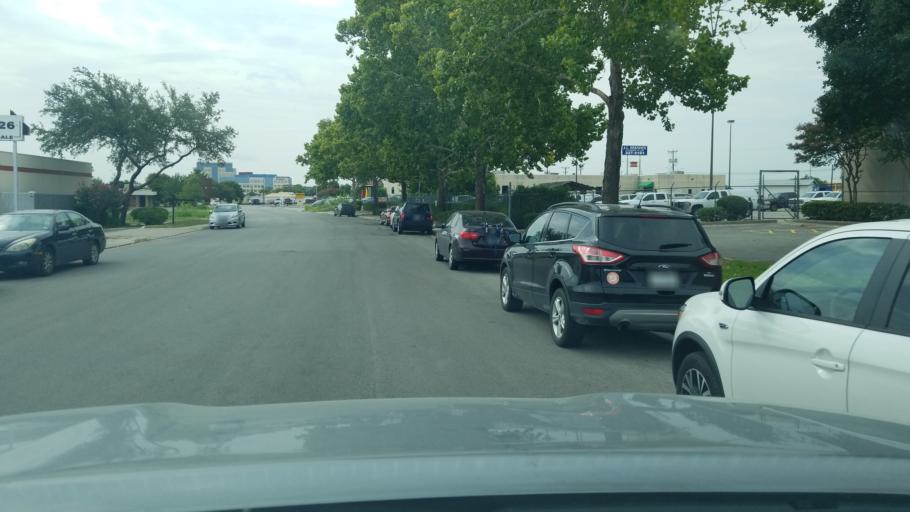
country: US
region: Texas
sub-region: Bexar County
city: Castle Hills
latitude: 29.5371
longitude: -98.4904
